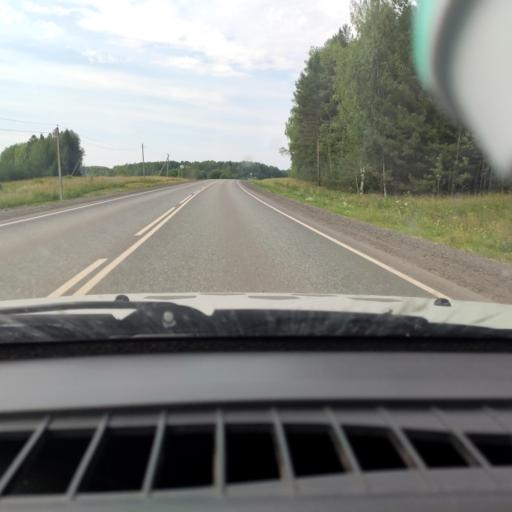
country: RU
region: Perm
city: Siva
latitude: 58.4911
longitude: 54.0553
